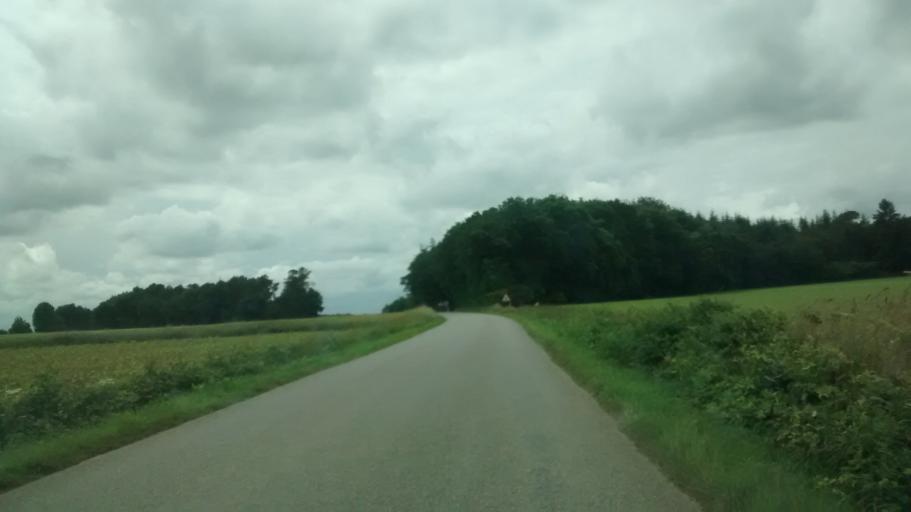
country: FR
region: Brittany
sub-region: Departement du Morbihan
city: Carentoir
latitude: 47.8271
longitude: -2.1737
